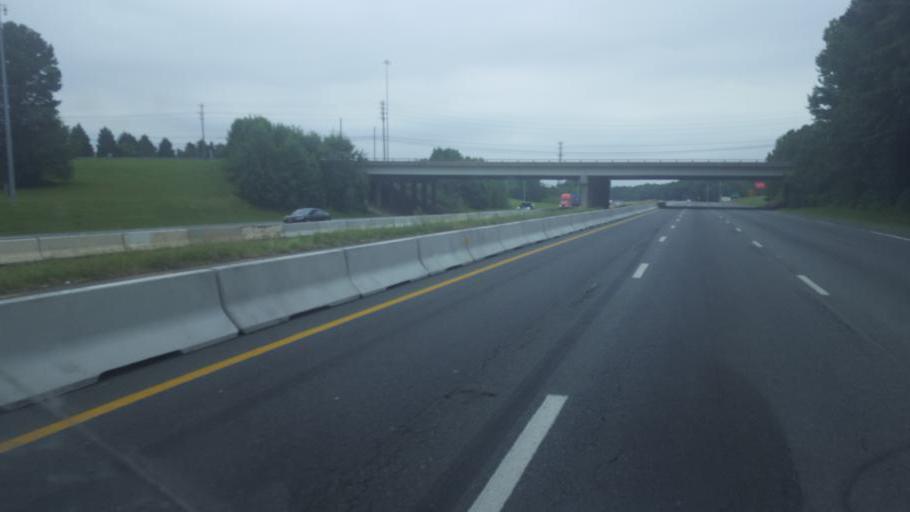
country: US
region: North Carolina
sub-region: Mecklenburg County
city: Charlotte
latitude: 35.3062
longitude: -80.8483
